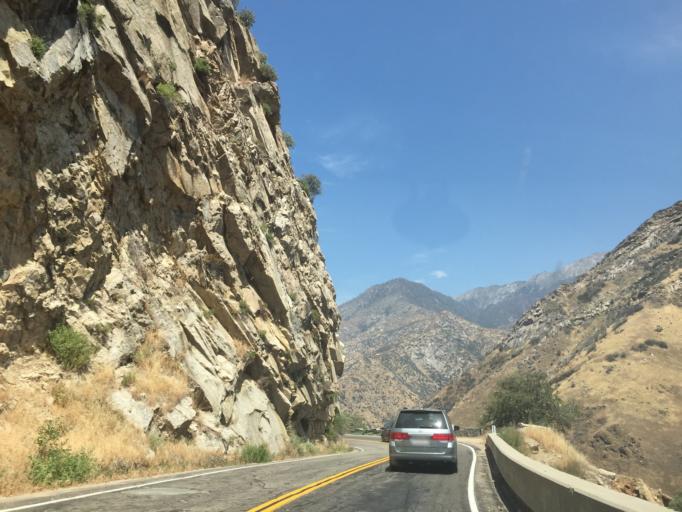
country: US
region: California
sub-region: Tulare County
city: Three Rivers
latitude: 36.8277
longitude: -118.8584
